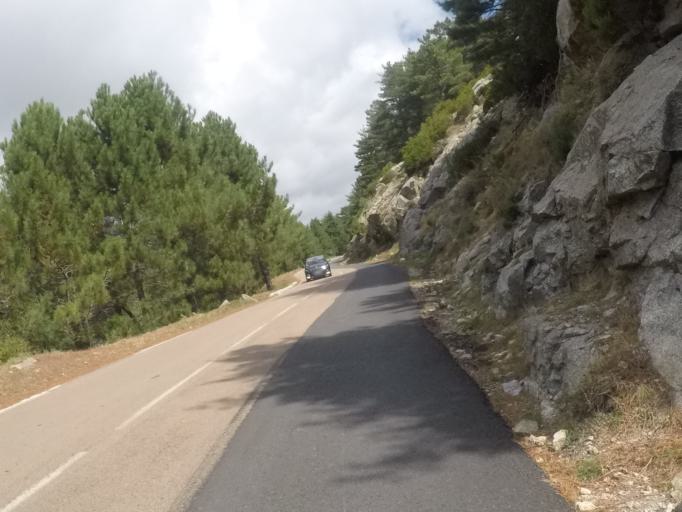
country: FR
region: Corsica
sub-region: Departement de la Corse-du-Sud
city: Zonza
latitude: 41.7860
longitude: 9.2198
